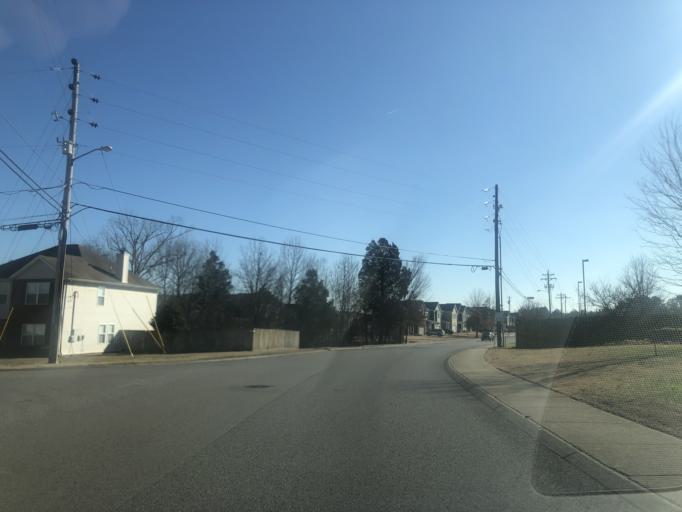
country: US
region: Tennessee
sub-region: Rutherford County
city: Smyrna
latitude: 35.9405
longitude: -86.5349
